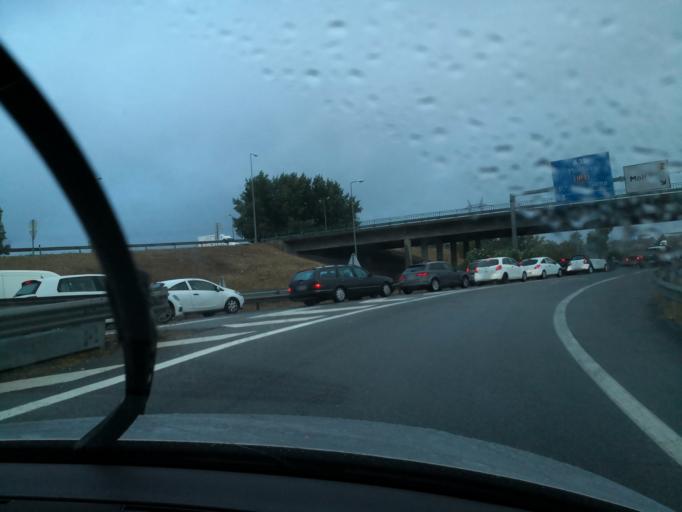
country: PT
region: Setubal
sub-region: Moita
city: Moita
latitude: 38.6434
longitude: -8.9753
